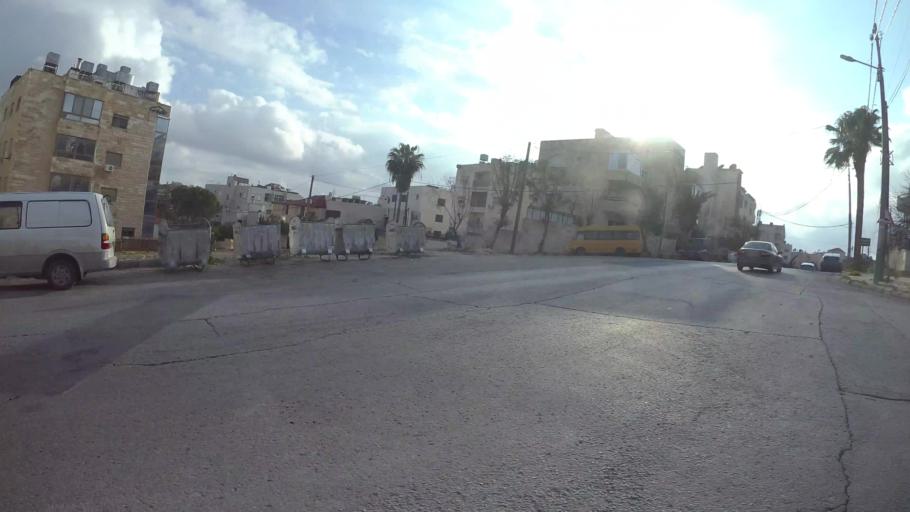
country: JO
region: Amman
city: Wadi as Sir
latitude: 31.9809
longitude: 35.8547
